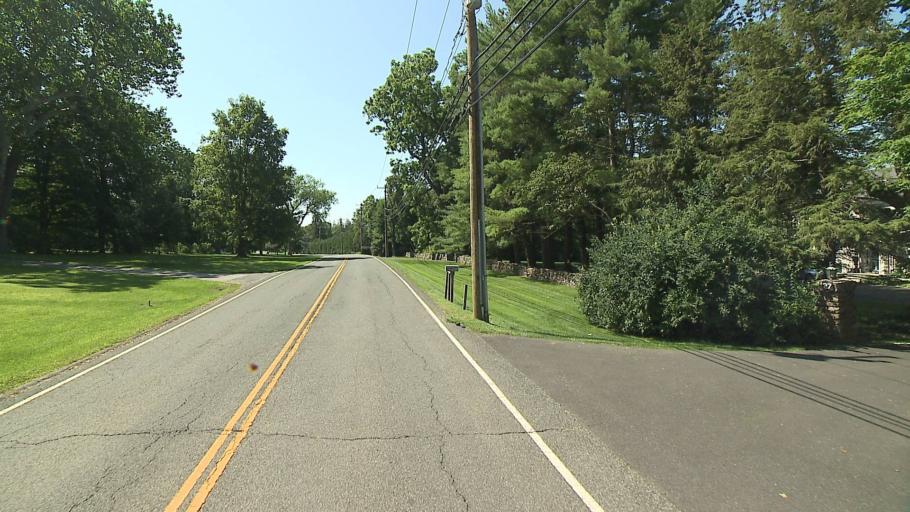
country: US
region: Connecticut
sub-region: Litchfield County
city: Kent
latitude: 41.8734
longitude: -73.4776
